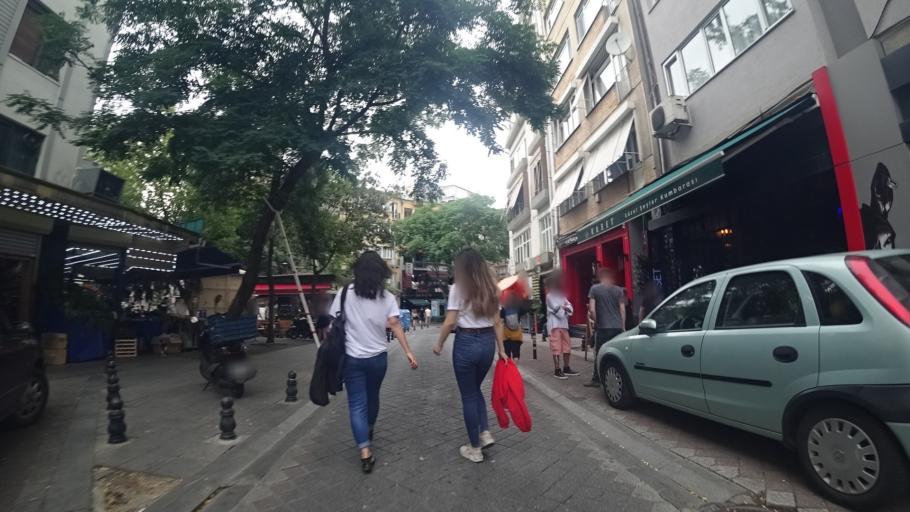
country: TR
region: Istanbul
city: UEskuedar
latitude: 40.9861
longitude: 29.0259
